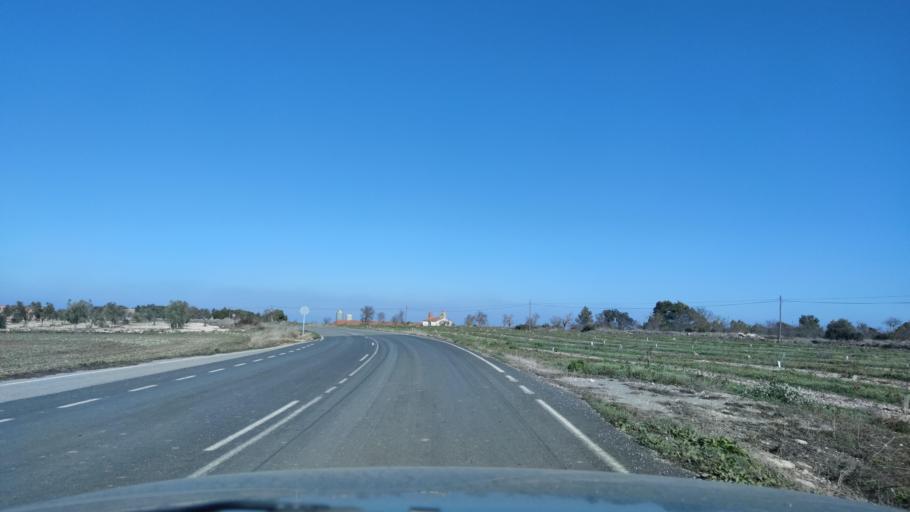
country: ES
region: Catalonia
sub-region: Provincia de Lleida
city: Maials
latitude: 41.3120
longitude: 0.4275
